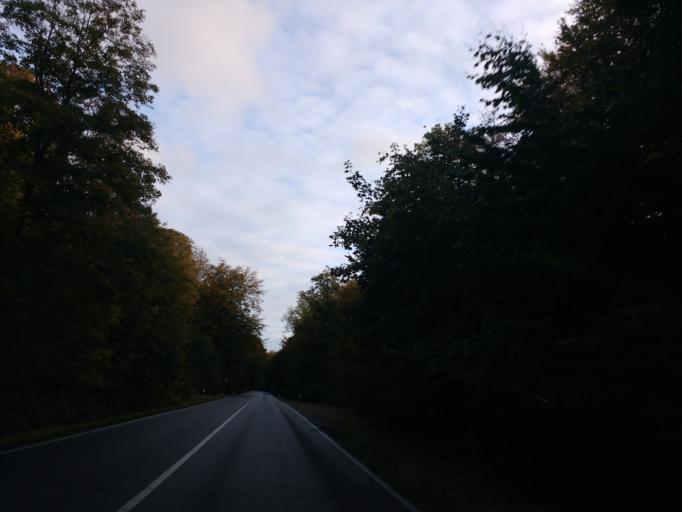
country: DE
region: Schleswig-Holstein
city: Schonwalde am Bungsberg
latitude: 54.1801
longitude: 10.7708
